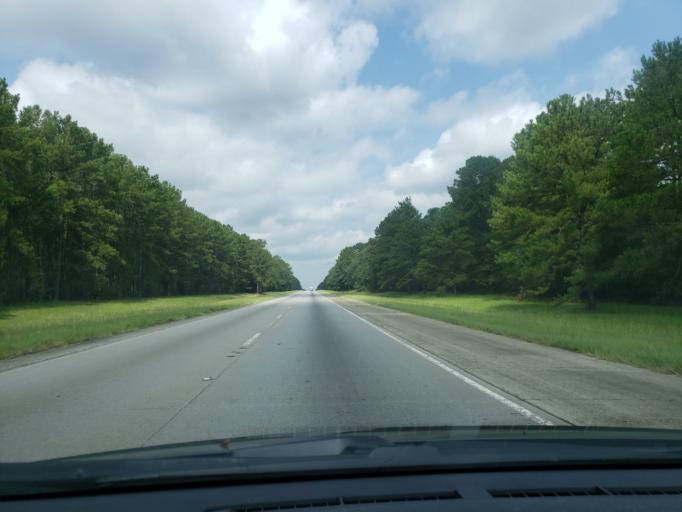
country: US
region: Georgia
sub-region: Emanuel County
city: Swainsboro
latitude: 32.4105
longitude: -82.3584
